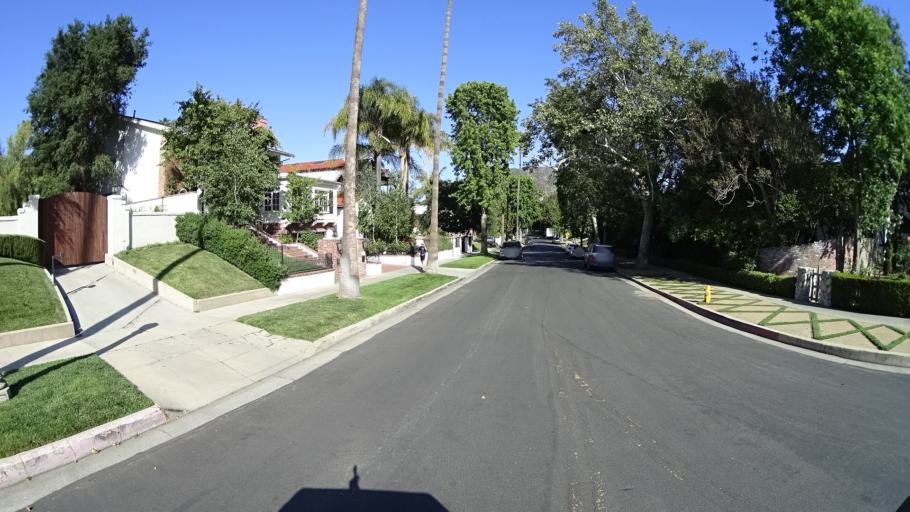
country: US
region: California
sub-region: Los Angeles County
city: Universal City
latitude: 34.1492
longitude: -118.3525
